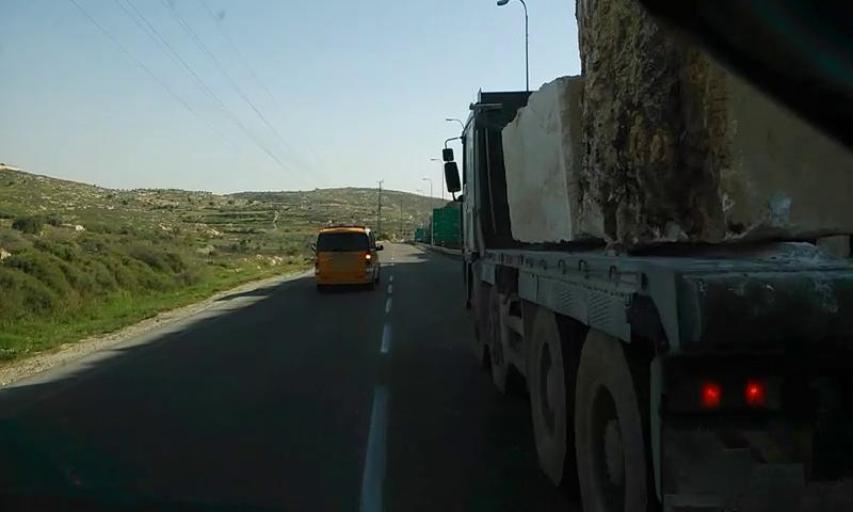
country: PS
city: Khallat ad Dar
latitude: 31.5062
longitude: 35.1330
